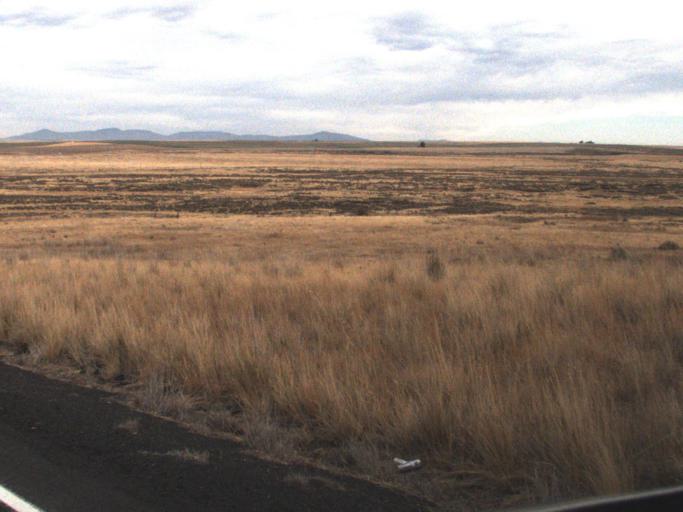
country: US
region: Washington
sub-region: Okanogan County
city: Coulee Dam
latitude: 47.6601
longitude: -118.7214
